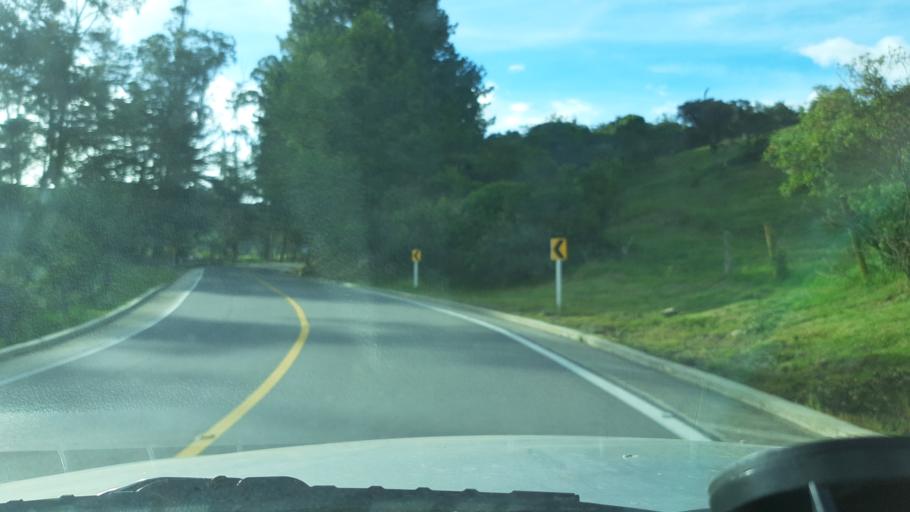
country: CO
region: Cundinamarca
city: Macheta
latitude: 5.0955
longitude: -73.6500
